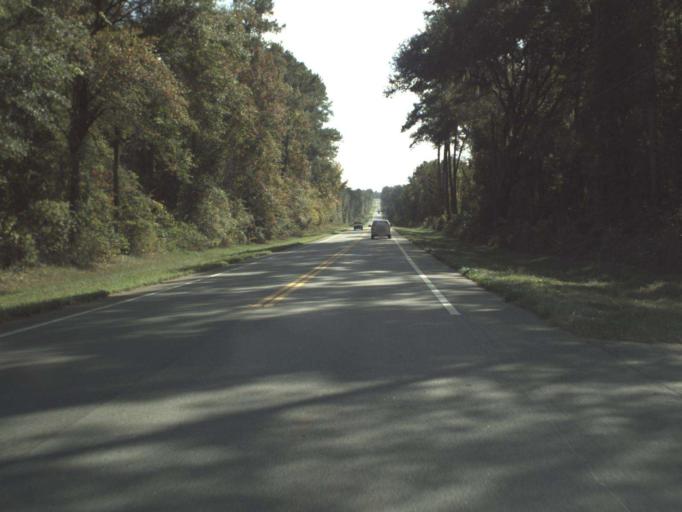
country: US
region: Florida
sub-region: Jefferson County
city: Monticello
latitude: 30.4326
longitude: -84.0196
